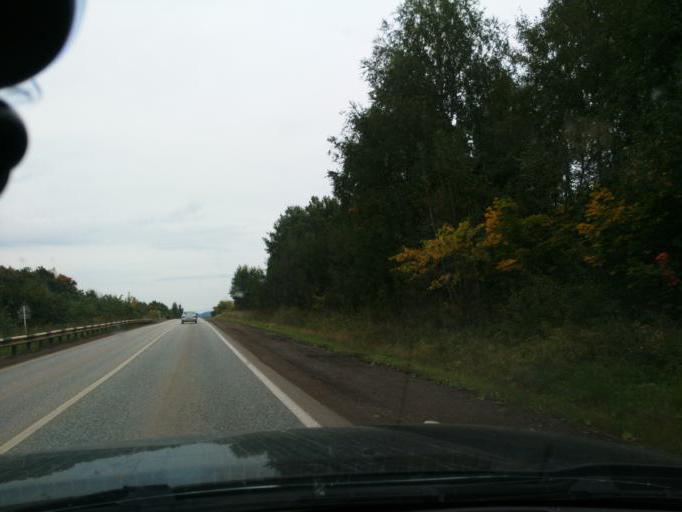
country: RU
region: Perm
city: Chernushka
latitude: 56.5849
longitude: 56.1461
